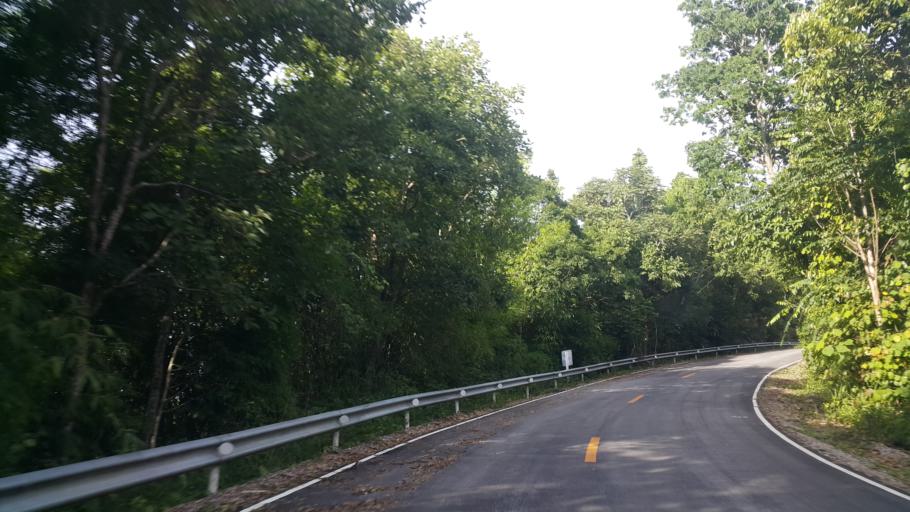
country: TH
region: Loei
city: Na Haeo
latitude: 17.5239
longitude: 101.0040
